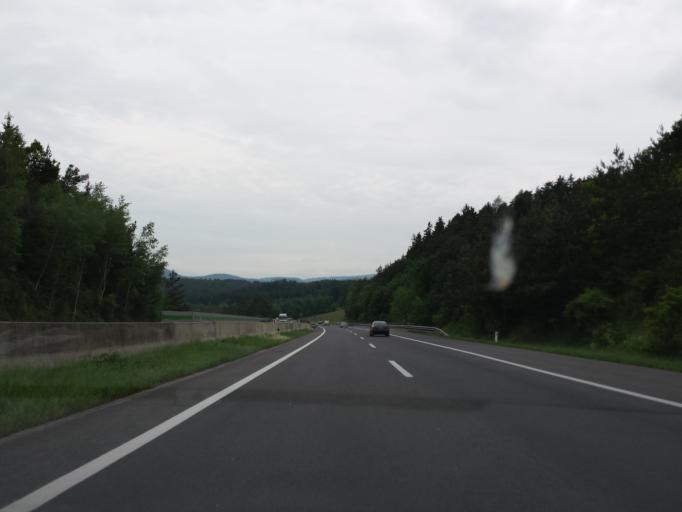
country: AT
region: Lower Austria
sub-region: Politischer Bezirk Neunkirchen
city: Seebenstein
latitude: 47.6855
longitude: 16.1249
